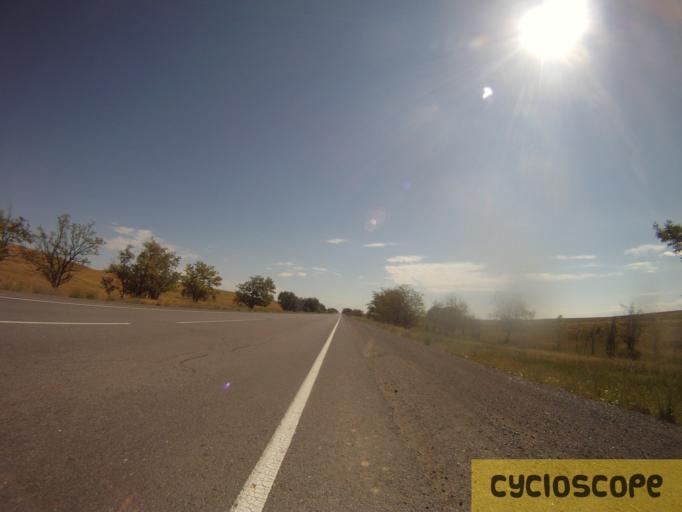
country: KG
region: Chuy
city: Bystrovka
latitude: 43.3200
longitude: 75.8009
